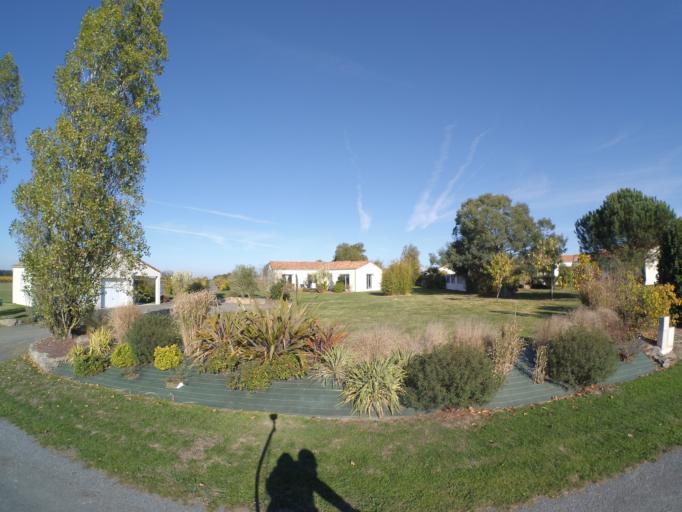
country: FR
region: Pays de la Loire
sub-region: Departement de la Loire-Atlantique
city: Saint-Lumine-de-Clisson
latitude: 47.0716
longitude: -1.3288
